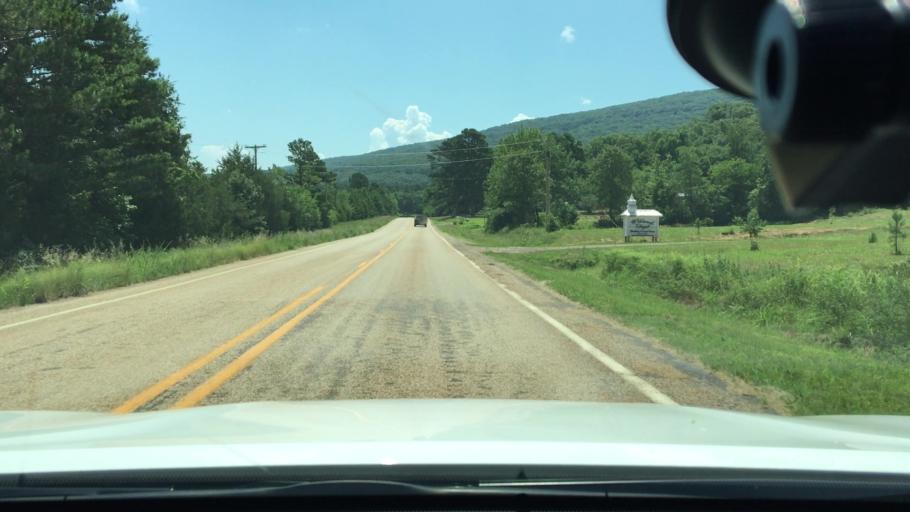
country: US
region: Arkansas
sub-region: Logan County
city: Paris
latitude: 35.1927
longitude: -93.6281
